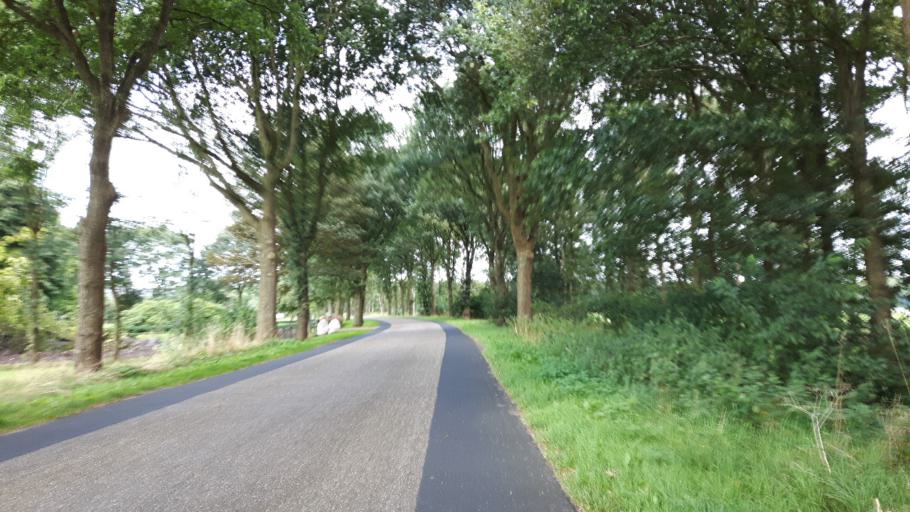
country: NL
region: Groningen
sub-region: Gemeente Leek
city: Leek
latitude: 53.0869
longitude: 6.3168
